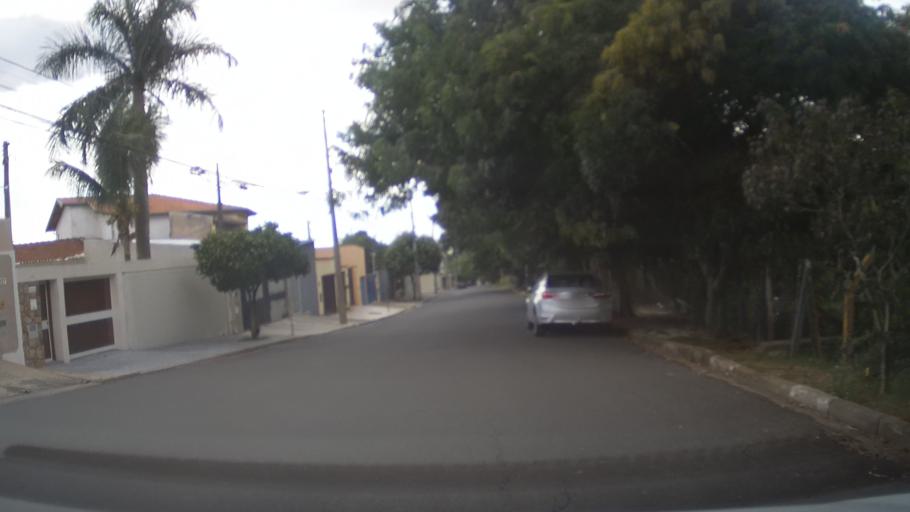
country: BR
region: Sao Paulo
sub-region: Campinas
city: Campinas
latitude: -22.8831
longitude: -47.1091
